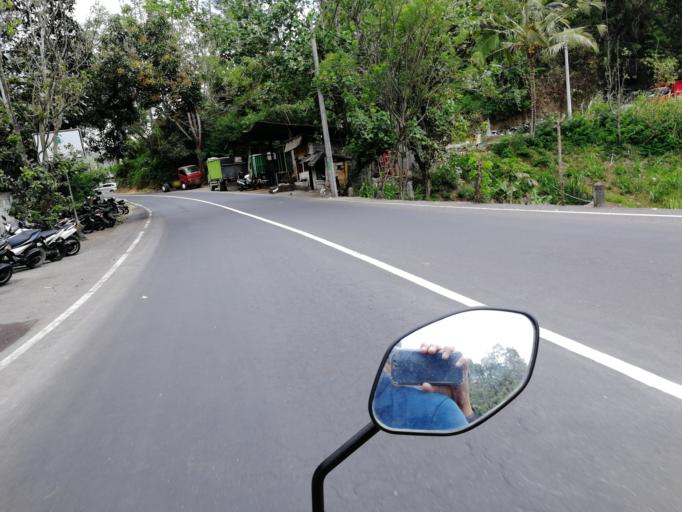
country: ID
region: Bali
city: Banjar Geriana Kangin
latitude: -8.4237
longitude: 115.4378
